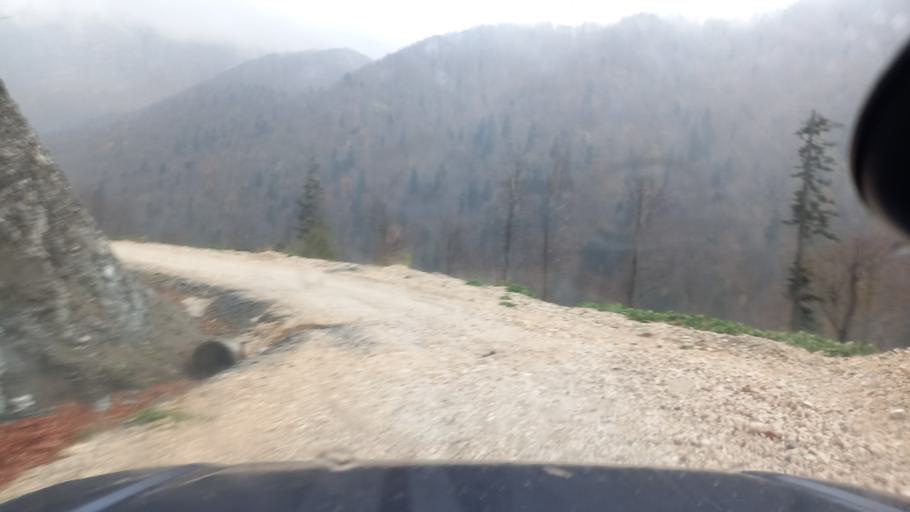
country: RU
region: Krasnodarskiy
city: Dagomys
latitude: 43.9793
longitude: 39.8511
